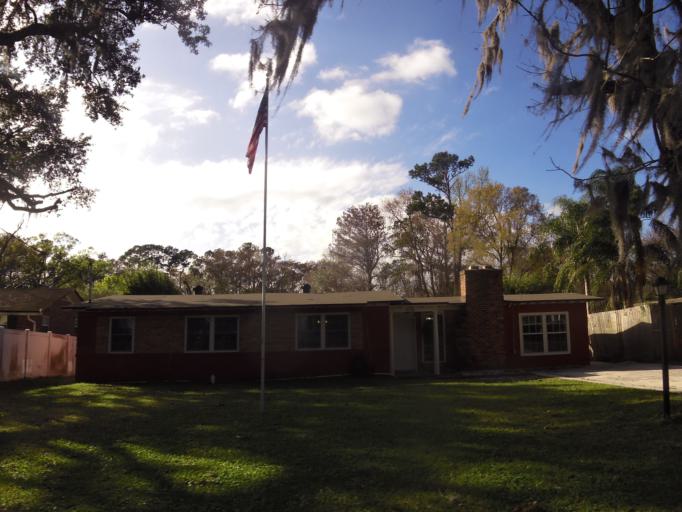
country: US
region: Florida
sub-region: Duval County
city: Jacksonville
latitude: 30.2963
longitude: -81.6182
